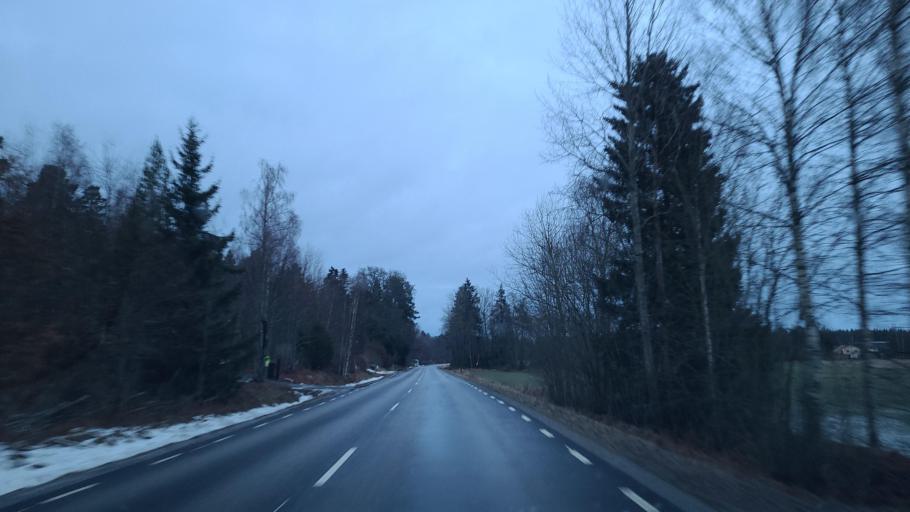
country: SE
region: Stockholm
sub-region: Norrtalje Kommun
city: Rimbo
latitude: 59.7228
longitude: 18.4751
